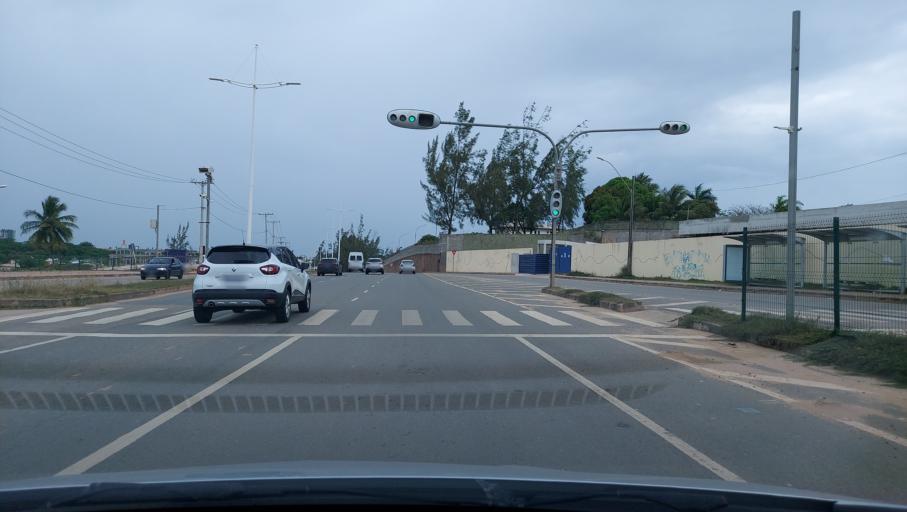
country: BR
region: Bahia
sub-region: Lauro De Freitas
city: Lauro de Freitas
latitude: -12.9401
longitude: -38.3865
